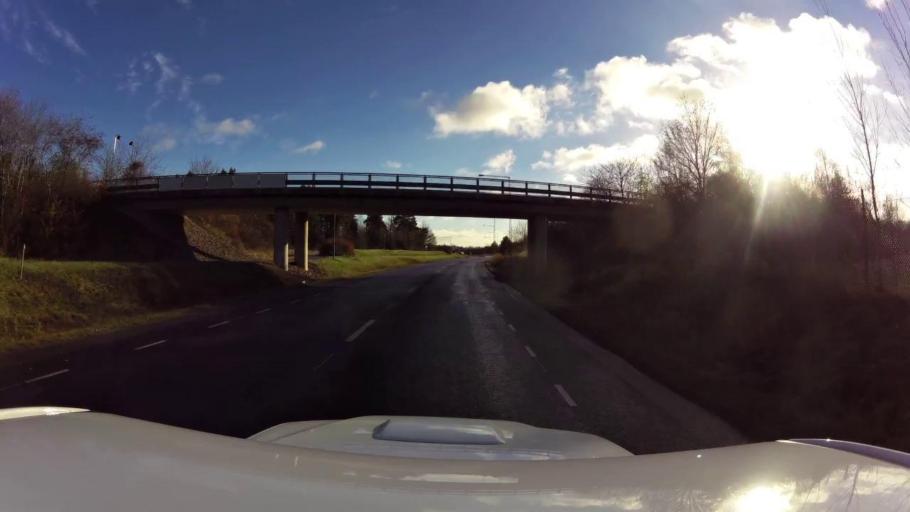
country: SE
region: OEstergoetland
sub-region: Linkopings Kommun
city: Linkoping
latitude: 58.3931
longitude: 15.6152
